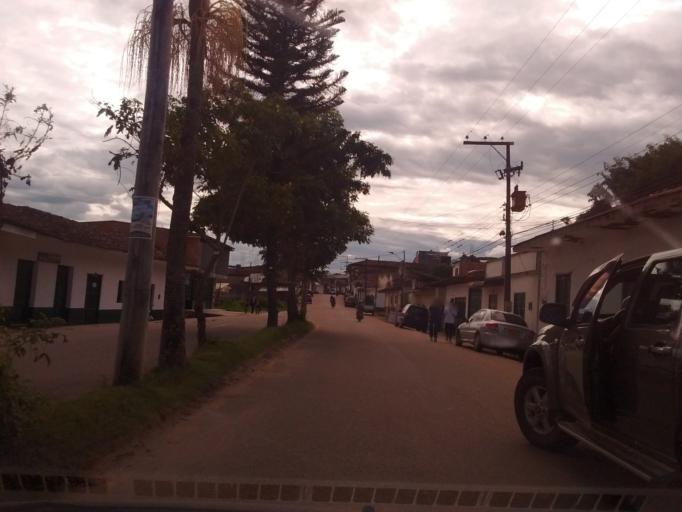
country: CO
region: Huila
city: San Agustin
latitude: 1.8793
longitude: -76.2675
